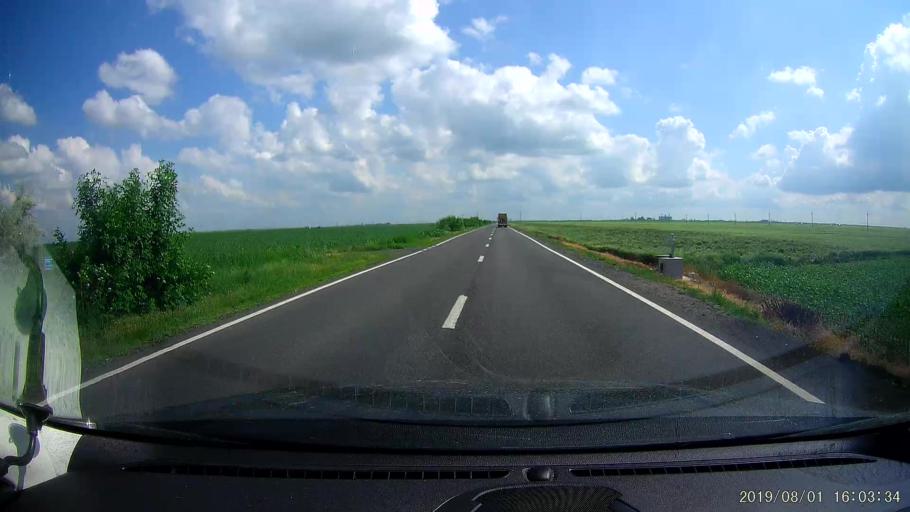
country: RO
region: Calarasi
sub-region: Comuna Dragalina
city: Drajna Noua
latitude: 44.4687
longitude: 27.3838
